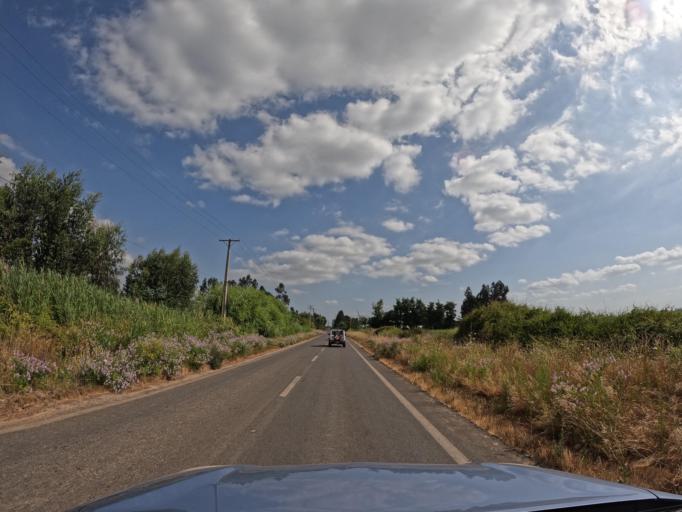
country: CL
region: Maule
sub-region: Provincia de Curico
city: Molina
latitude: -35.1974
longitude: -71.2974
